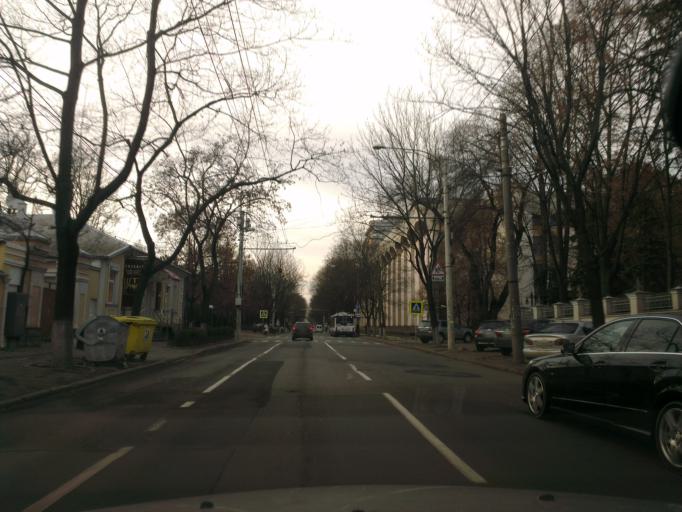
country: MD
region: Chisinau
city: Chisinau
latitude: 47.0231
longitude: 28.8259
